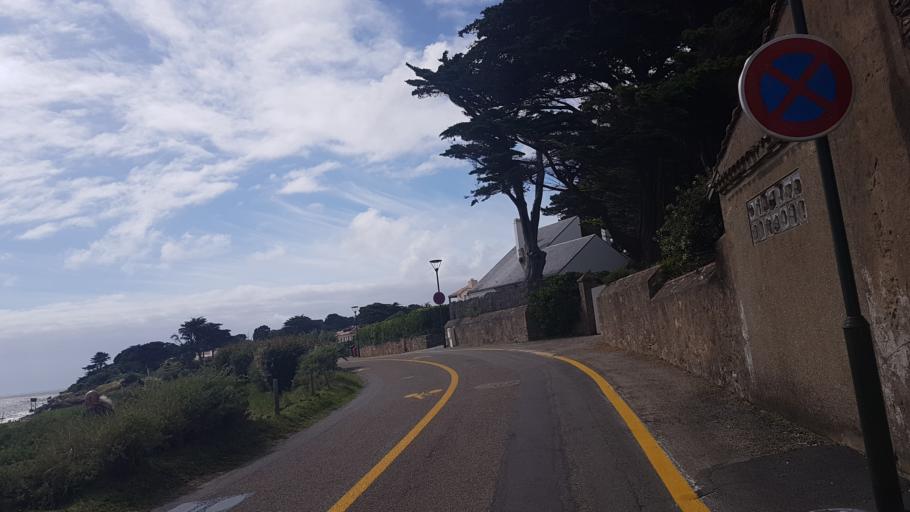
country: FR
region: Pays de la Loire
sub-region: Departement de la Loire-Atlantique
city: La Plaine-sur-Mer
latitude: 47.1124
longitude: -2.1447
